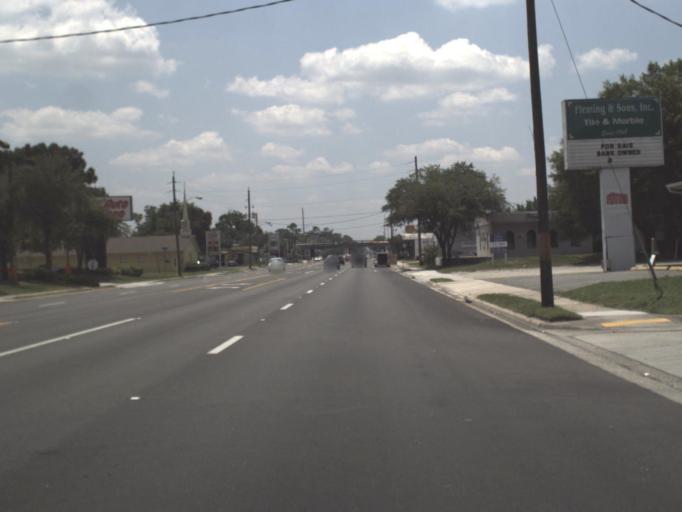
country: US
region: Florida
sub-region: Duval County
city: Jacksonville
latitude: 30.3211
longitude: -81.7309
